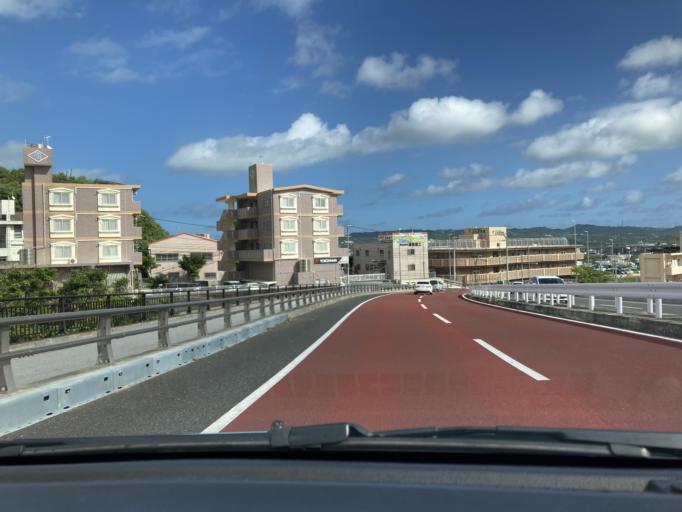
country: JP
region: Okinawa
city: Naha-shi
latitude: 26.2017
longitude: 127.7285
